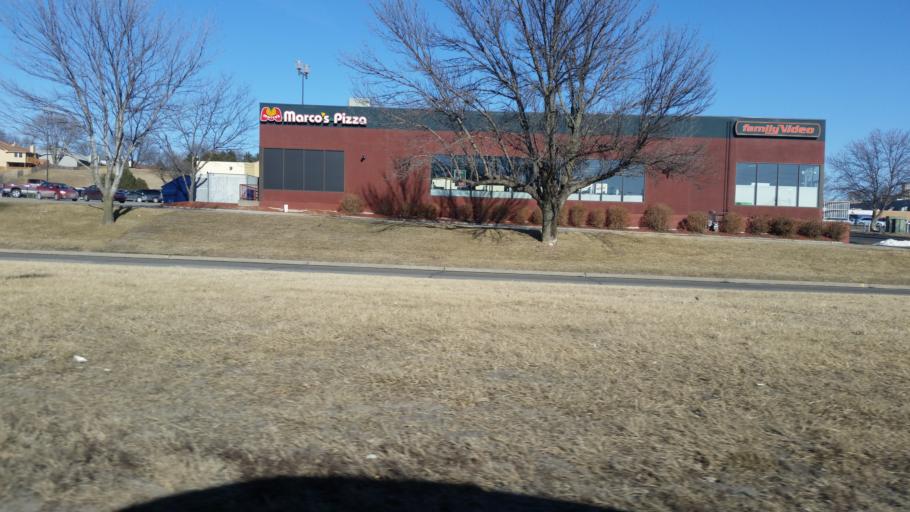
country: US
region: Nebraska
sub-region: Sarpy County
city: Bellevue
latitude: 41.1541
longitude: -95.9185
